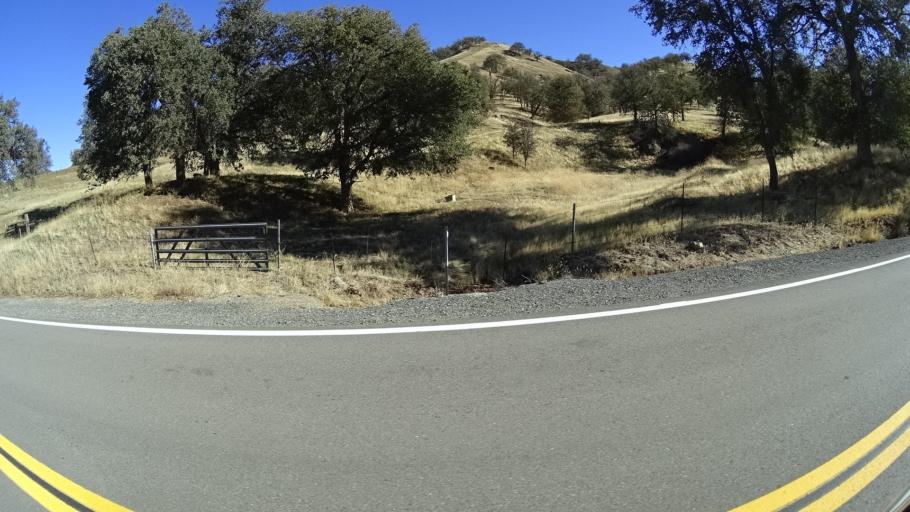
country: US
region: California
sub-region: Kern County
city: Alta Sierra
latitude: 35.7230
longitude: -118.6963
